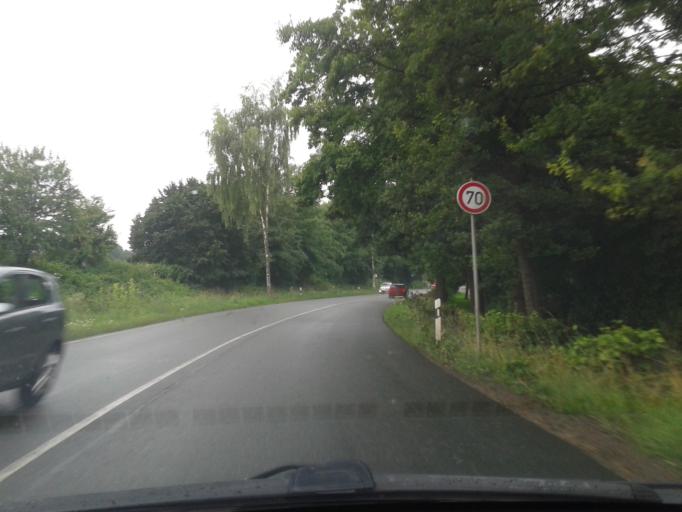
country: DE
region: North Rhine-Westphalia
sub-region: Regierungsbezirk Detmold
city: Detmold
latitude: 51.9681
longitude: 8.8955
